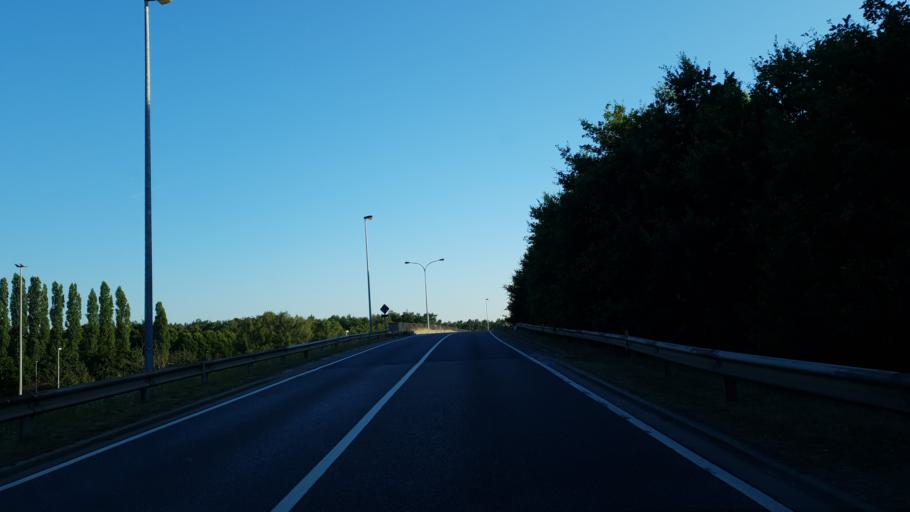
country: BE
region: Flanders
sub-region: Provincie Antwerpen
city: Beerse
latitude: 51.2849
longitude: 4.8561
